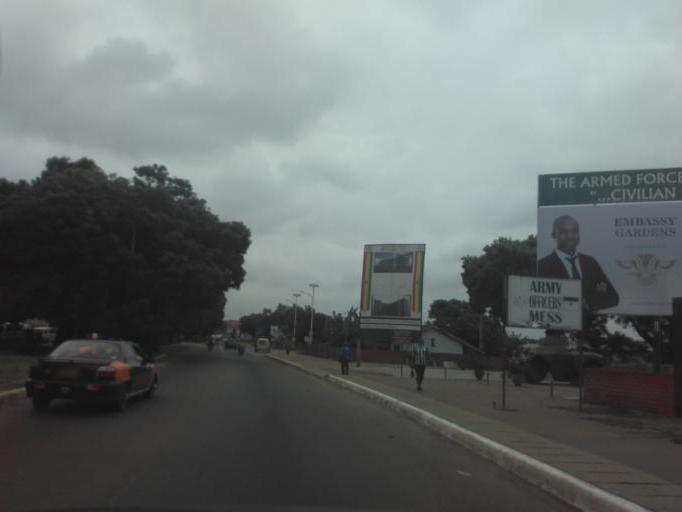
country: GH
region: Greater Accra
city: Accra
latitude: 5.5871
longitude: -0.1832
